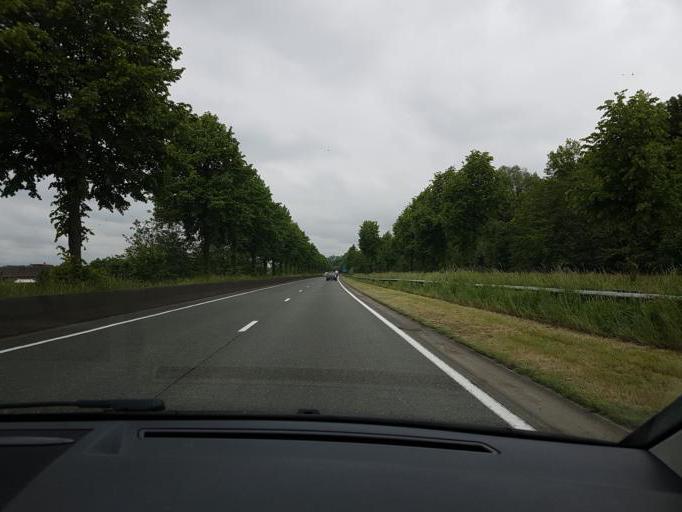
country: BE
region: Flanders
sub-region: Provincie Oost-Vlaanderen
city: Gent
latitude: 51.0421
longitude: 3.6799
